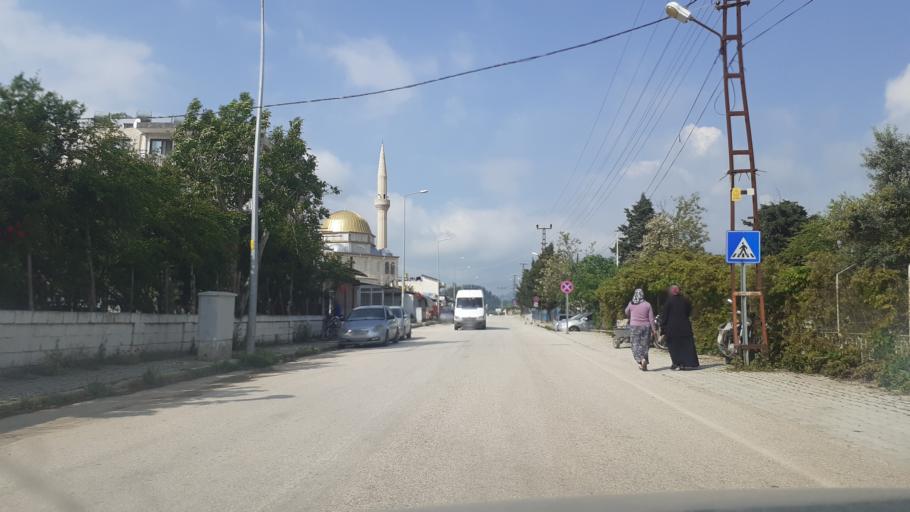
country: TR
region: Hatay
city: Yayladagi
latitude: 35.9073
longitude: 36.0523
